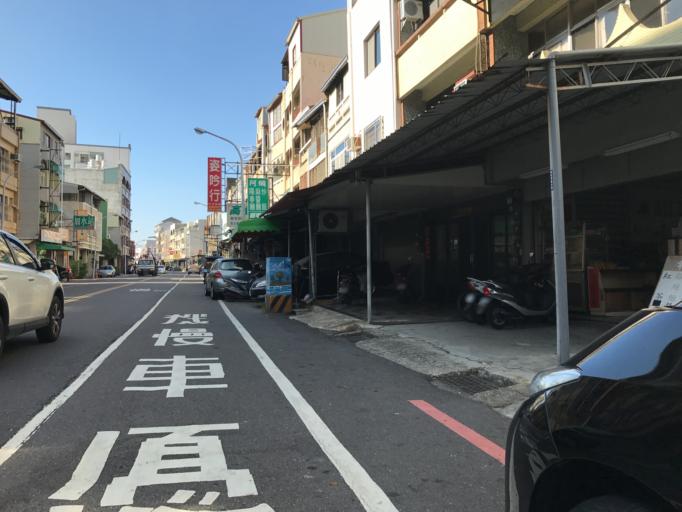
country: TW
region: Taiwan
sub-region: Tainan
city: Tainan
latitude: 22.9996
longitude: 120.1678
